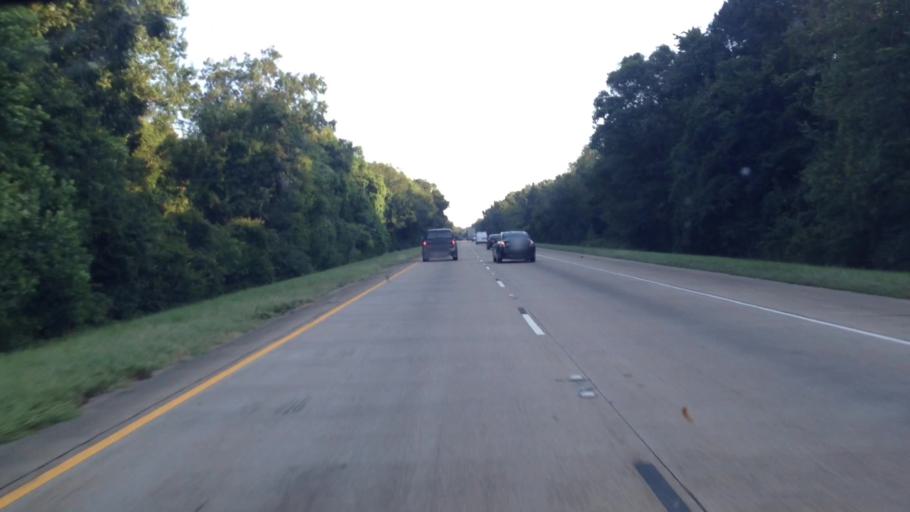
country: US
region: Louisiana
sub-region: Ascension Parish
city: Prairieville
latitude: 30.2922
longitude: -90.9907
